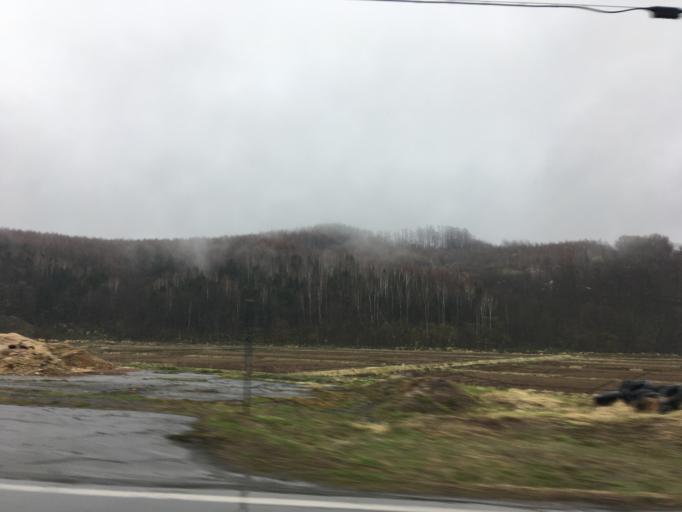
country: JP
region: Hokkaido
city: Nayoro
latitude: 44.0912
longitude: 142.4240
